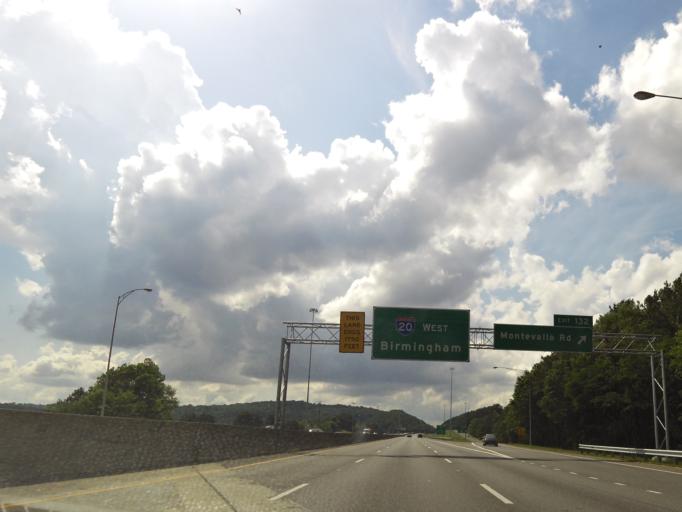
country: US
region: Alabama
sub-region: Jefferson County
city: Irondale
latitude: 33.5313
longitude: -86.7120
